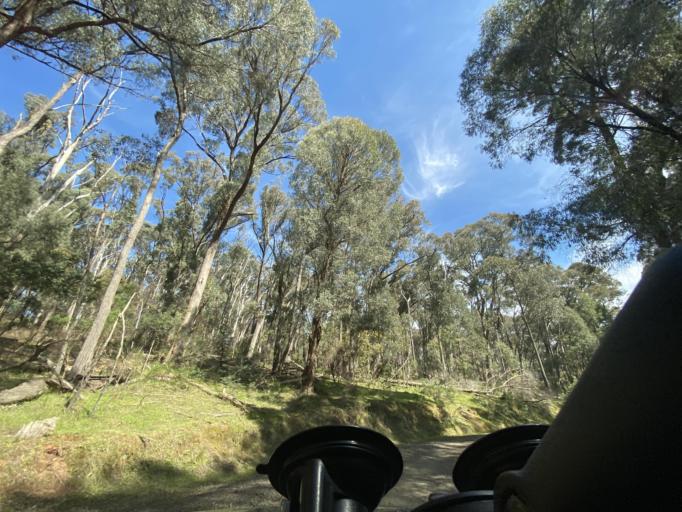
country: AU
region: Victoria
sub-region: Mansfield
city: Mansfield
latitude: -36.8127
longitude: 146.1041
